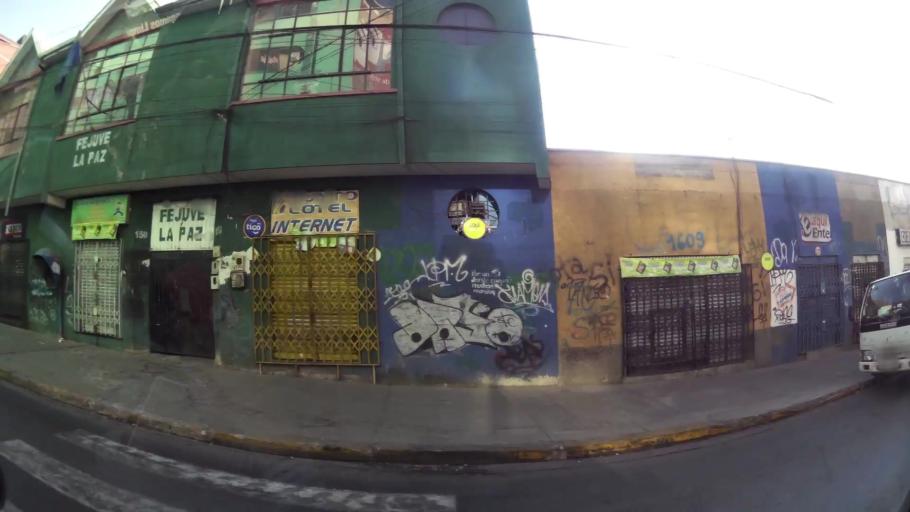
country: BO
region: La Paz
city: La Paz
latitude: -16.5014
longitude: -68.1321
